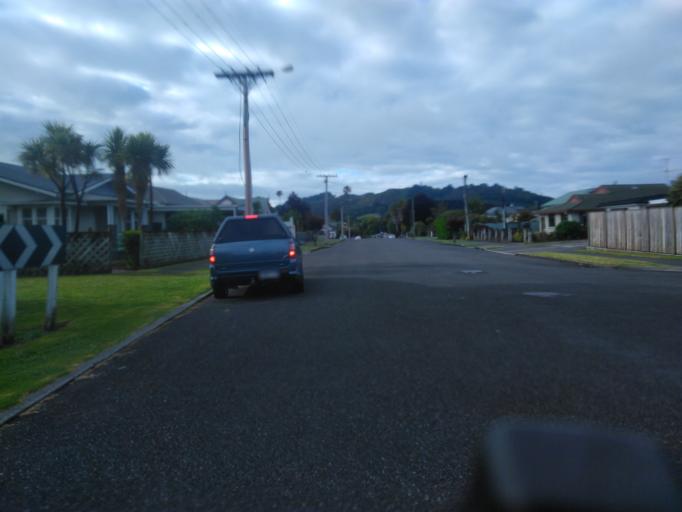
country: NZ
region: Gisborne
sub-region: Gisborne District
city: Gisborne
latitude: -38.6624
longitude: 178.0316
